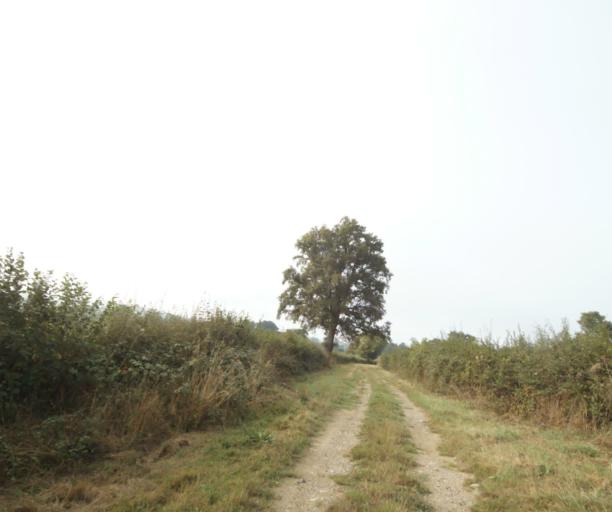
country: FR
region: Bourgogne
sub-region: Departement de Saone-et-Loire
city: Charolles
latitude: 46.4680
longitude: 4.3048
